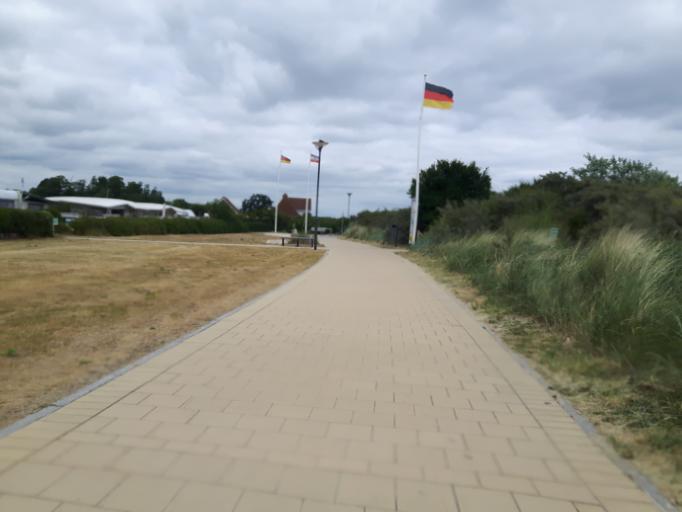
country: DE
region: Schleswig-Holstein
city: Schashagen
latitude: 54.0977
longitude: 10.8930
